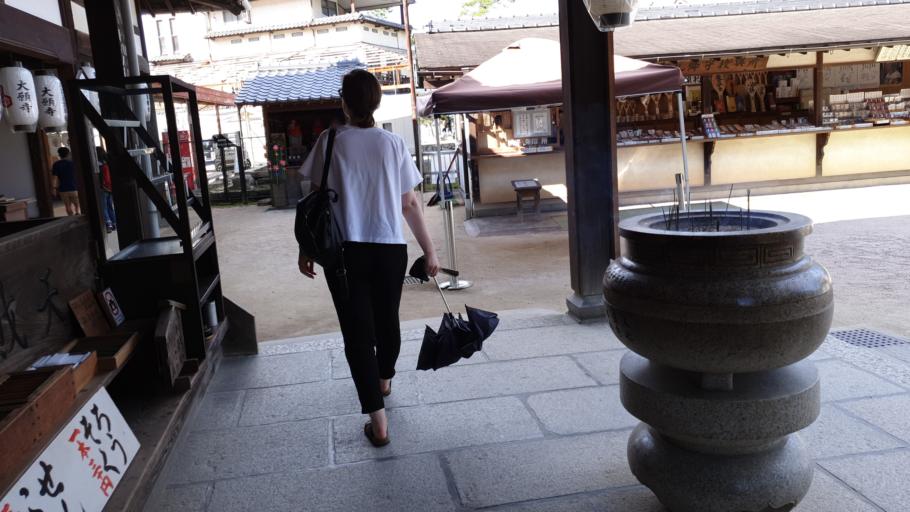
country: JP
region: Hiroshima
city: Miyajima
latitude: 34.2954
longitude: 132.3183
